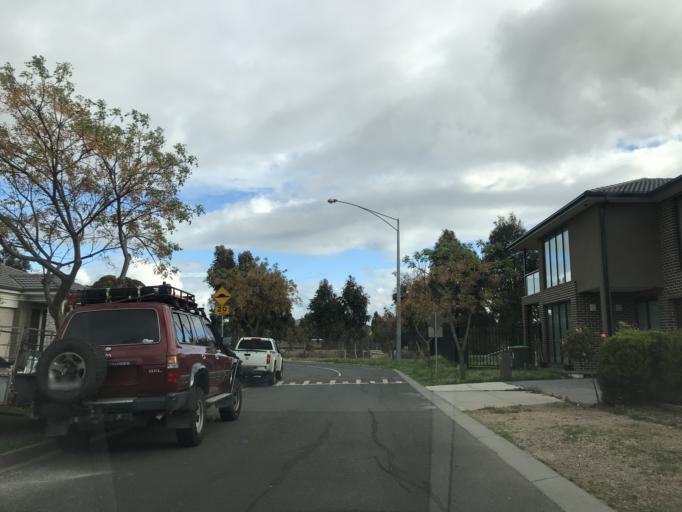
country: AU
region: Victoria
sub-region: Brimbank
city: Sunshine West
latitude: -37.7949
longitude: 144.8020
